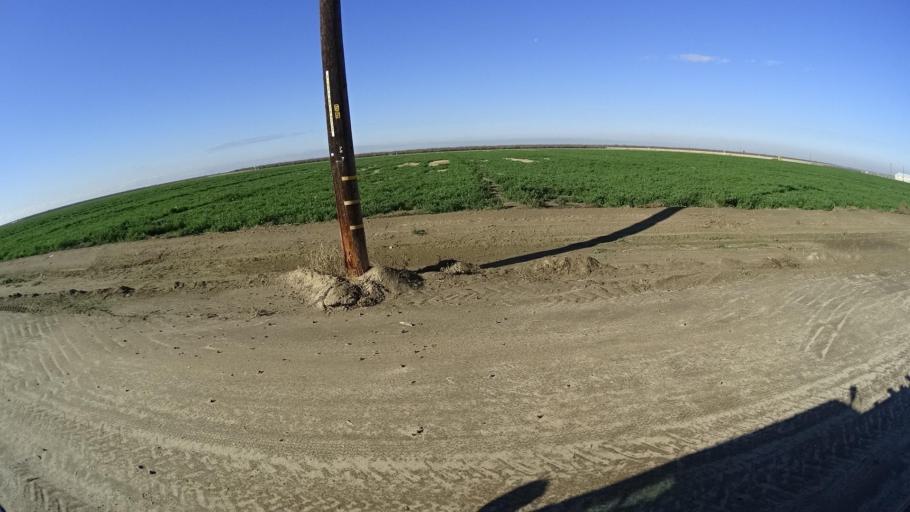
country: US
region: California
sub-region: Kern County
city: McFarland
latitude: 35.6790
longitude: -119.2765
